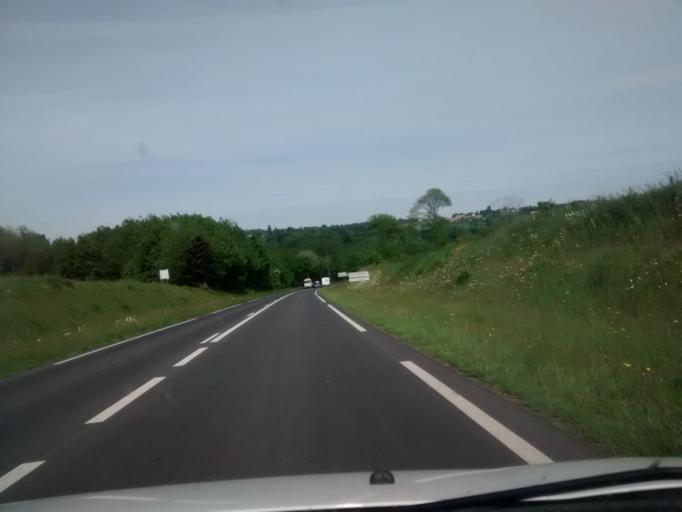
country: FR
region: Brittany
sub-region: Departement d'Ille-et-Vilaine
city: Antrain
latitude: 48.4553
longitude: -1.4880
